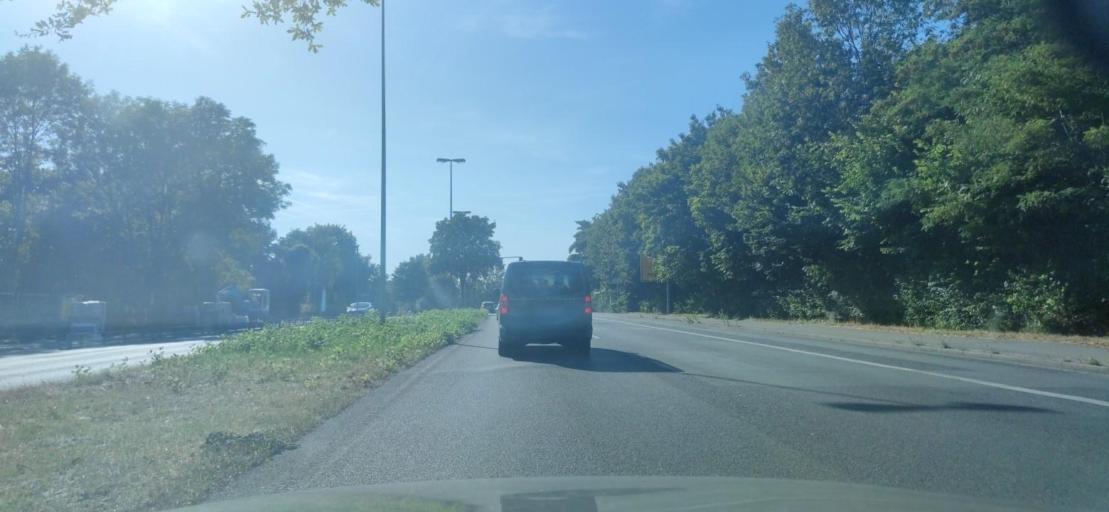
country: DE
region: North Rhine-Westphalia
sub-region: Regierungsbezirk Dusseldorf
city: Essen
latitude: 51.4854
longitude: 6.9709
